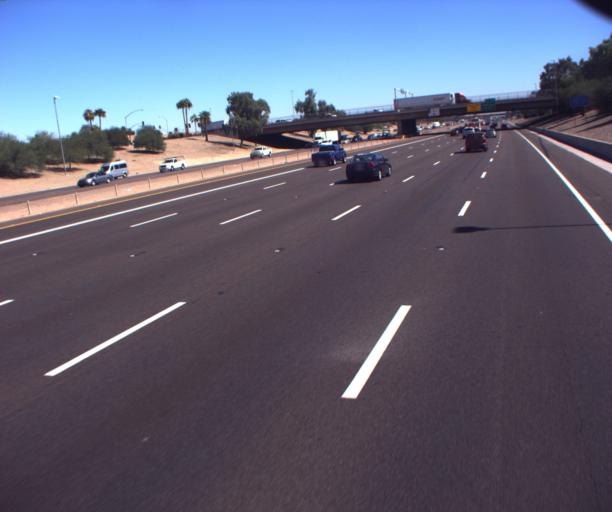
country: US
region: Arizona
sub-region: Maricopa County
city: Tolleson
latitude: 33.4620
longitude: -112.2403
